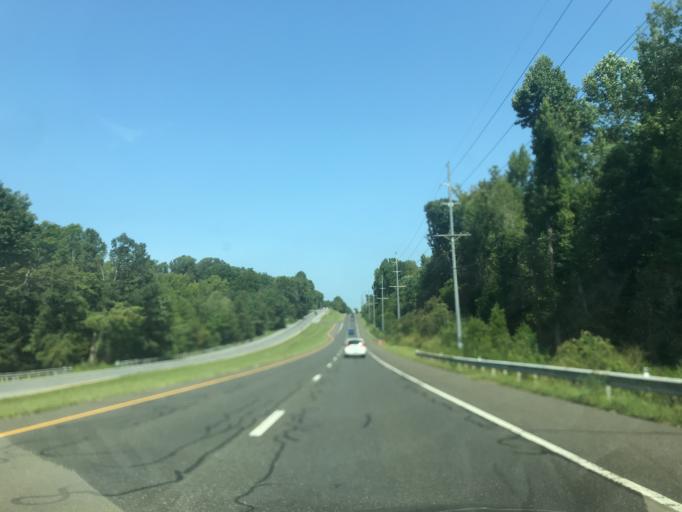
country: US
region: Maryland
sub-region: Calvert County
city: Dunkirk Town Center
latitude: 38.6976
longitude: -76.6434
